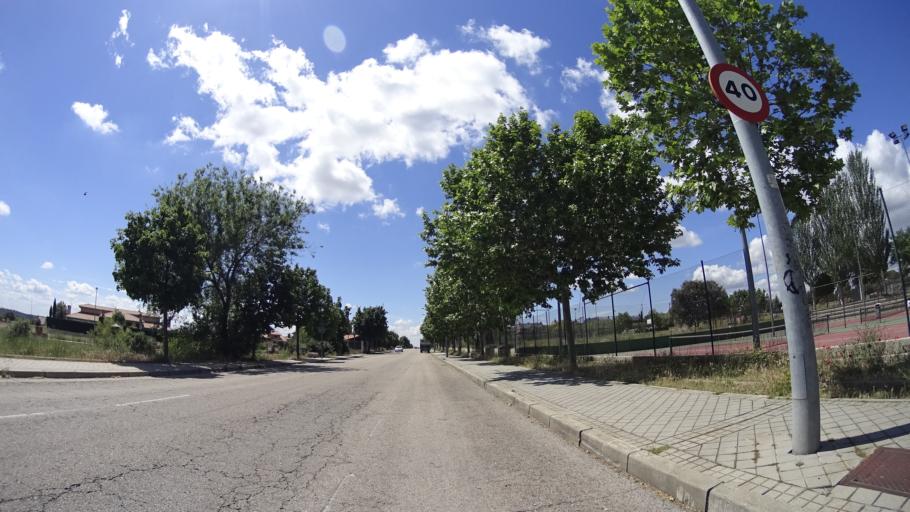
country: ES
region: Madrid
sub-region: Provincia de Madrid
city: Colmenarejo
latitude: 40.5513
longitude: -4.0115
